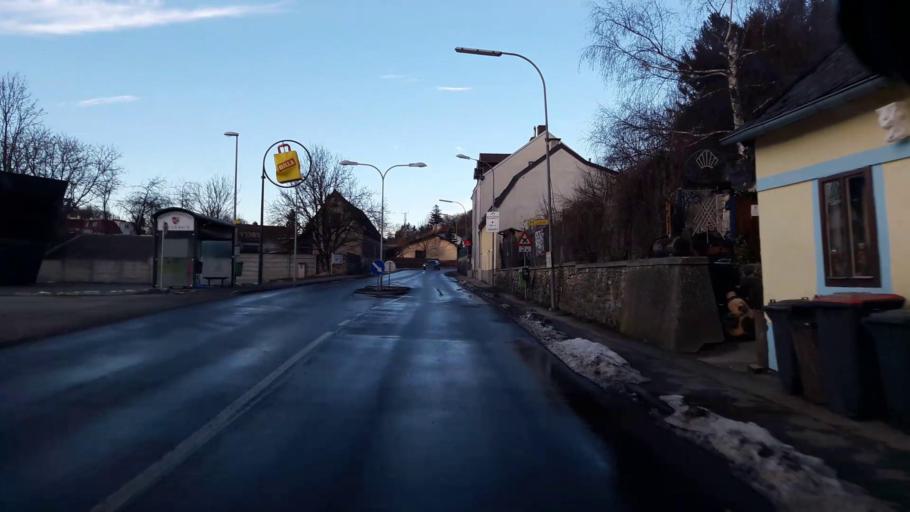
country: AT
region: Lower Austria
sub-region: Politischer Bezirk Wien-Umgebung
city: Mauerbach
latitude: 48.2431
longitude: 16.1681
